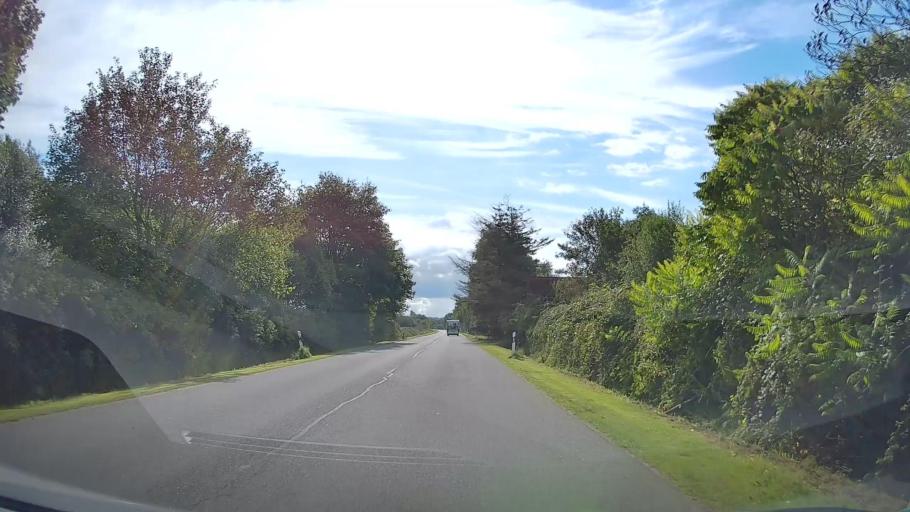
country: DE
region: Schleswig-Holstein
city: Glucksburg
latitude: 54.8653
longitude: 9.5930
